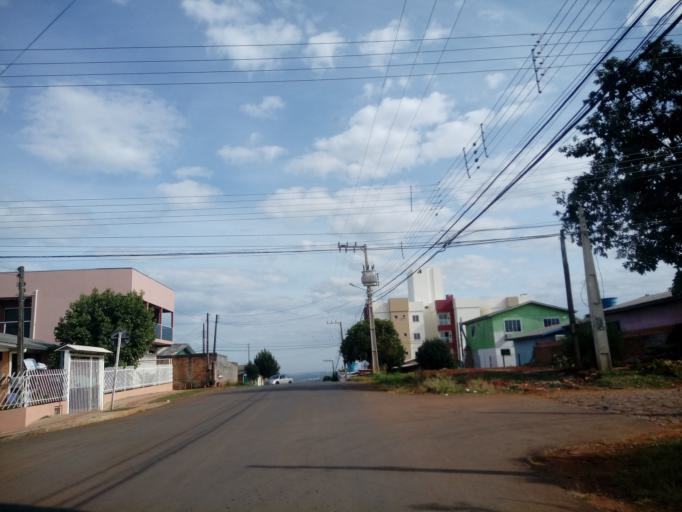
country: BR
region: Santa Catarina
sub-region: Chapeco
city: Chapeco
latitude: -27.1215
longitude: -52.6256
